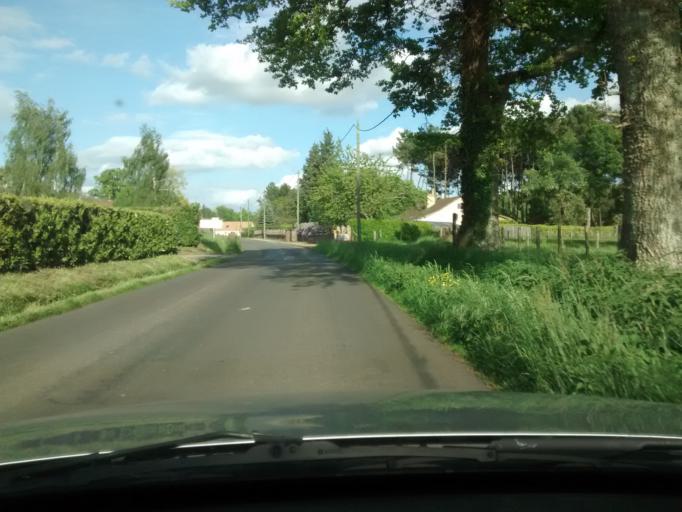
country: FR
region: Pays de la Loire
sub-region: Departement de la Sarthe
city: Brette-les-Pins
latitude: 47.9382
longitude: 0.3476
